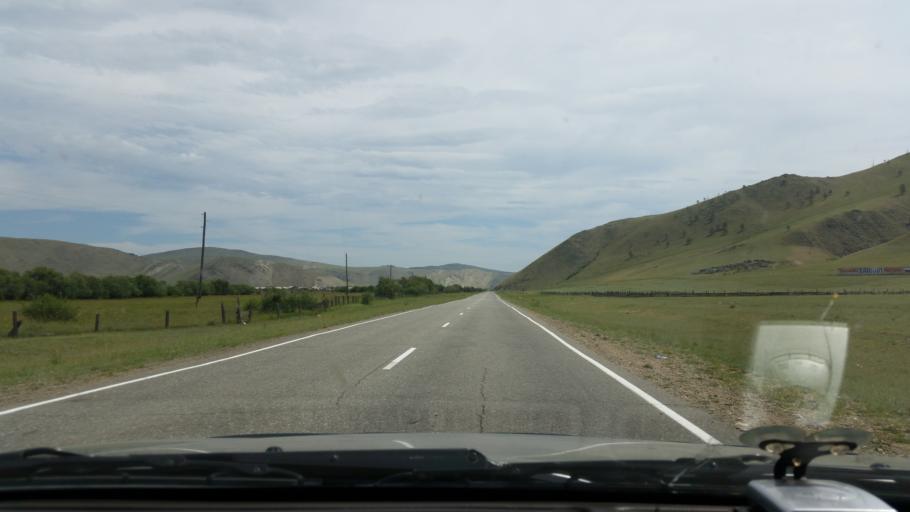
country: RU
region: Irkutsk
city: Yelantsy
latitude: 52.8058
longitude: 106.4479
